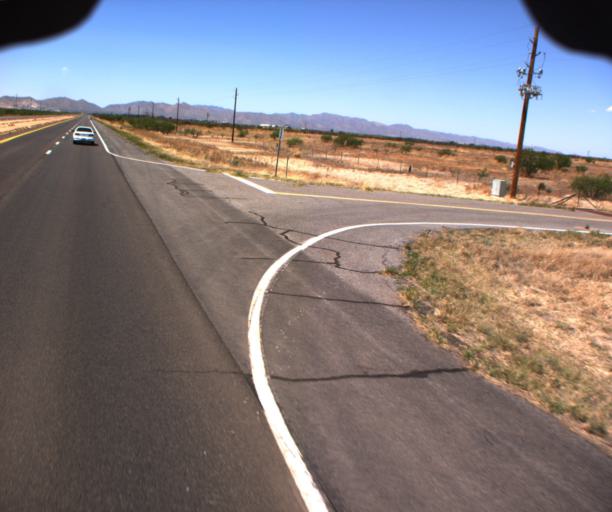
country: US
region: Arizona
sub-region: Cochise County
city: Pirtleville
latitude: 31.3603
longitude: -109.6592
